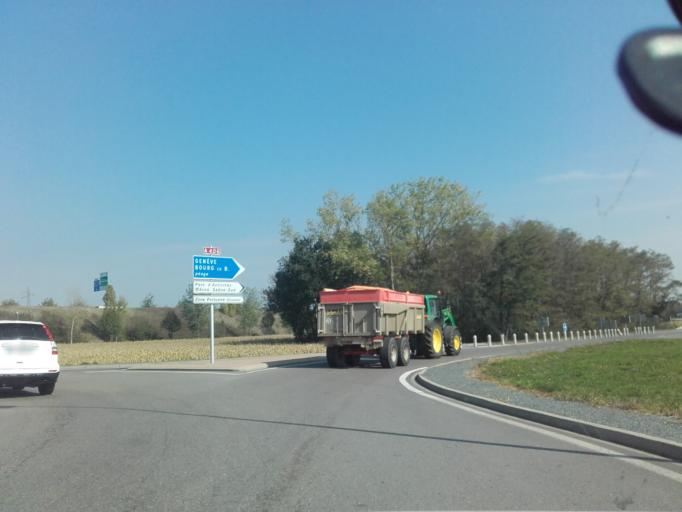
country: FR
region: Bourgogne
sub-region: Departement de Saone-et-Loire
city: Creches-sur-Saone
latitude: 46.2761
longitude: 4.8011
